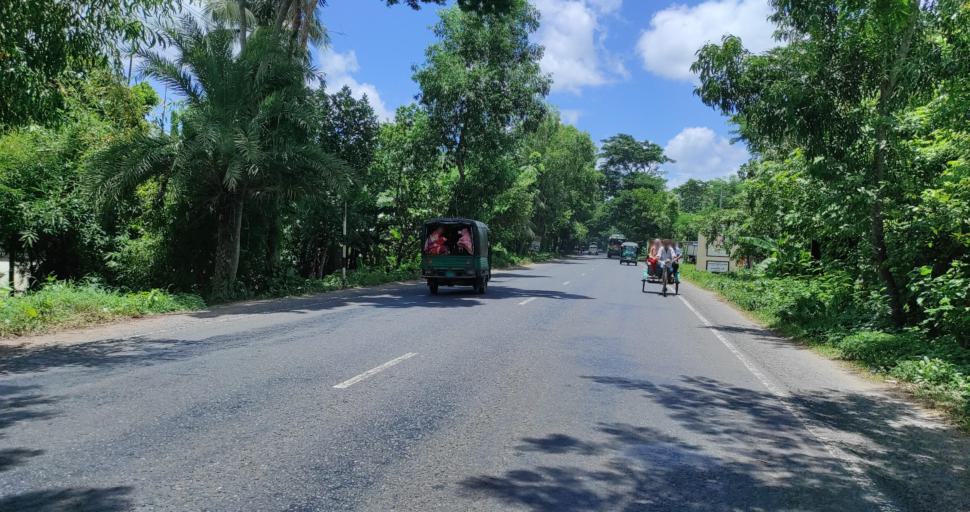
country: BD
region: Barisal
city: Gaurnadi
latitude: 22.8353
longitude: 90.2536
